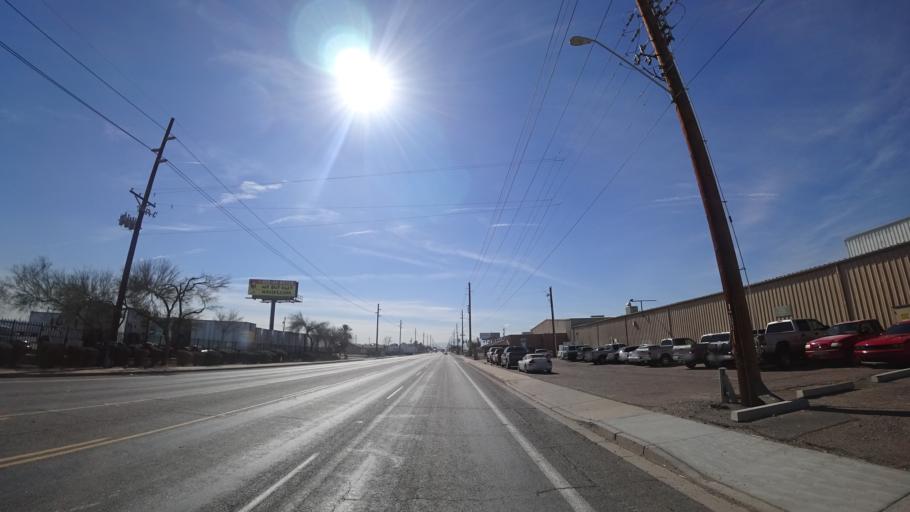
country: US
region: Arizona
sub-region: Maricopa County
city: Tolleson
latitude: 33.4418
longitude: -112.1866
